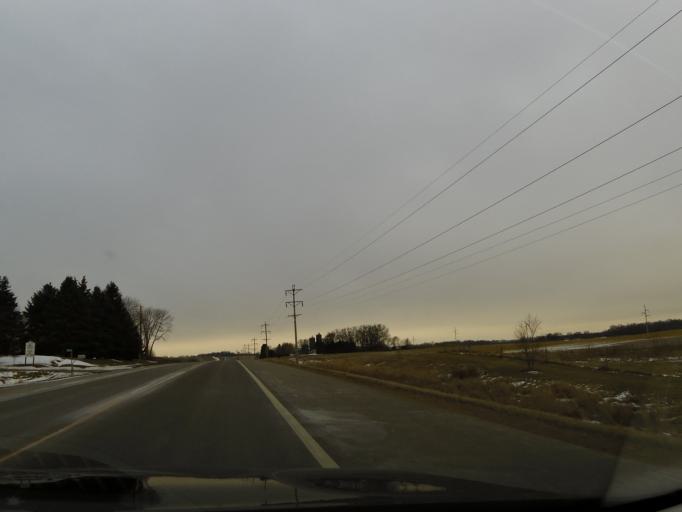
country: US
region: Minnesota
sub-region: Carver County
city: Waconia
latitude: 44.8975
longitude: -93.8185
